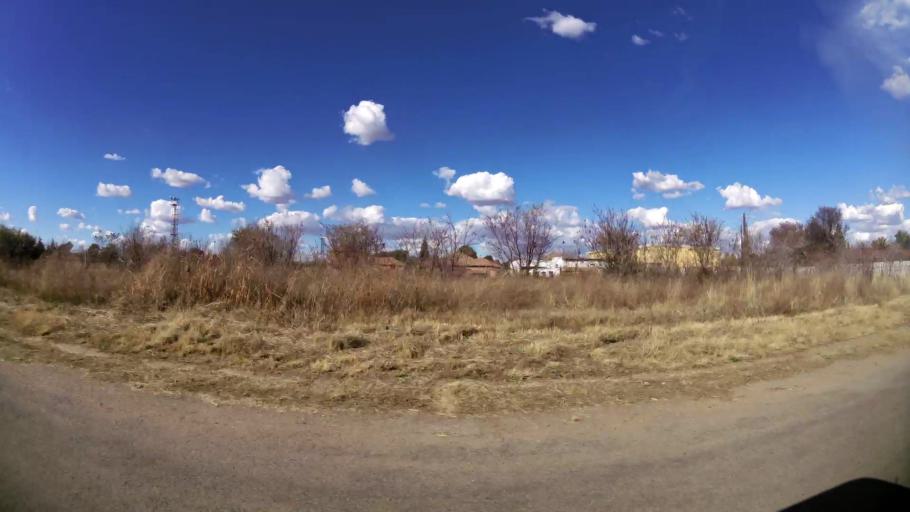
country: ZA
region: North-West
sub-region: Dr Kenneth Kaunda District Municipality
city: Klerksdorp
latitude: -26.8164
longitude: 26.6504
